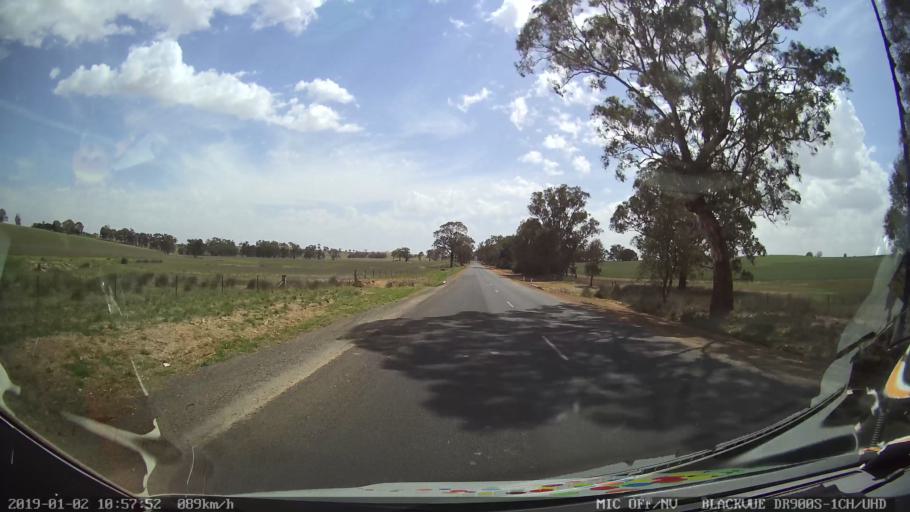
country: AU
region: New South Wales
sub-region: Cootamundra
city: Cootamundra
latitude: -34.6305
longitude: 148.2859
